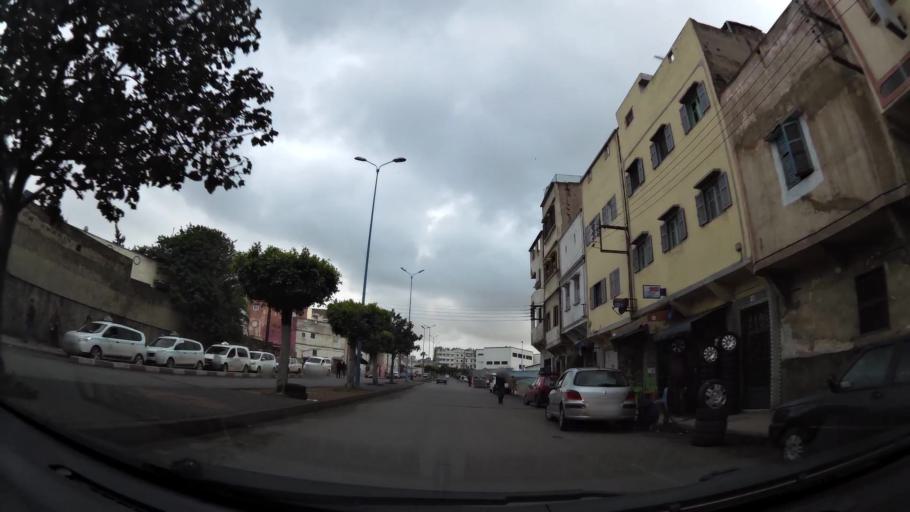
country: MA
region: Grand Casablanca
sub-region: Casablanca
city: Casablanca
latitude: 33.5666
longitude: -7.6026
